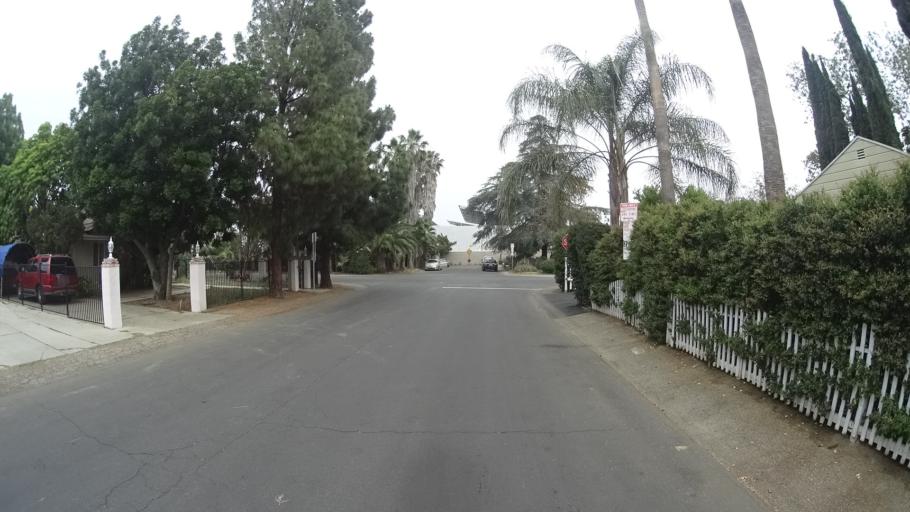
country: US
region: California
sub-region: Los Angeles County
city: Van Nuys
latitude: 34.1789
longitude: -118.4514
